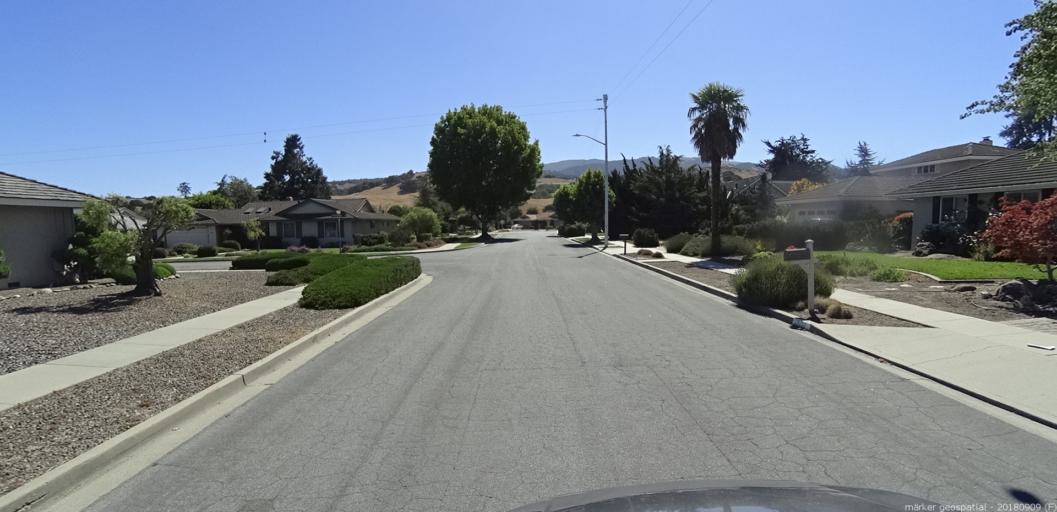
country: US
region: California
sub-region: Monterey County
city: Salinas
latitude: 36.5994
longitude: -121.7013
